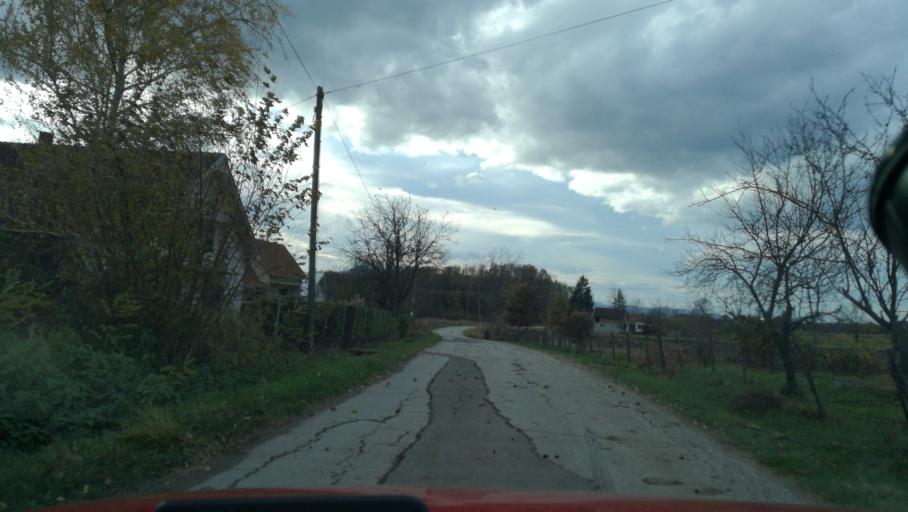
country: RS
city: Prislonica
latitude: 43.9094
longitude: 20.4374
